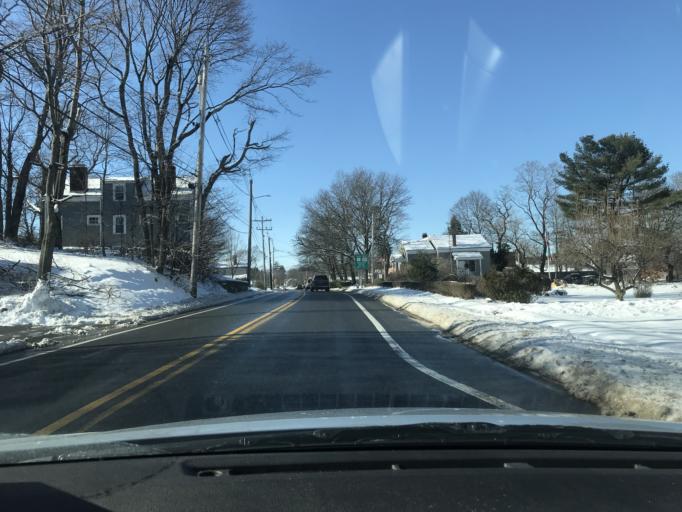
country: US
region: Massachusetts
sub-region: Essex County
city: Saugus
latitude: 42.5141
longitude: -71.0004
